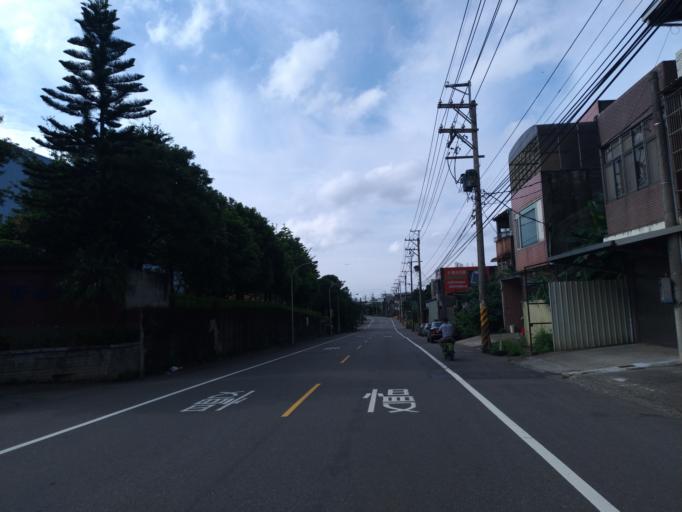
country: TW
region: Taiwan
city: Daxi
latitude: 24.9340
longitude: 121.1705
